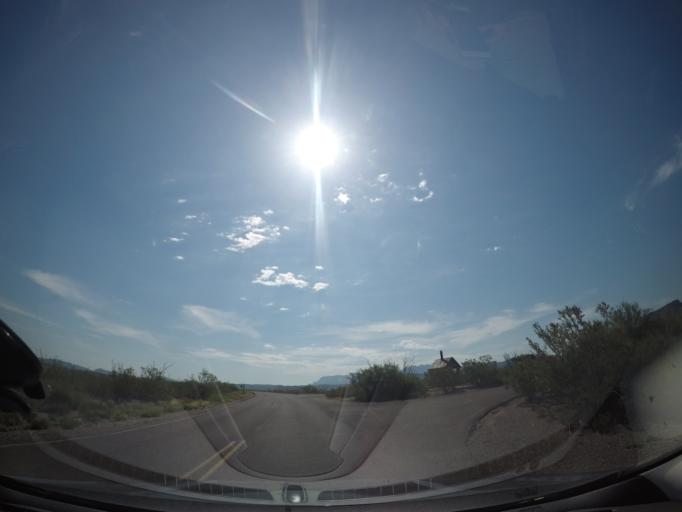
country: US
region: Texas
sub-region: Presidio County
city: Presidio
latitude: 29.2938
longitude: -103.4957
